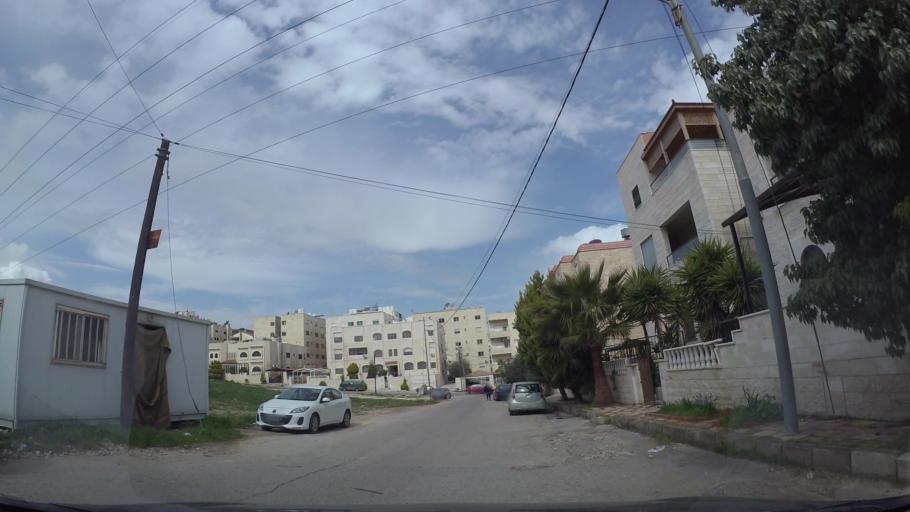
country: JO
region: Amman
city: Amman
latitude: 31.9960
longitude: 35.9369
